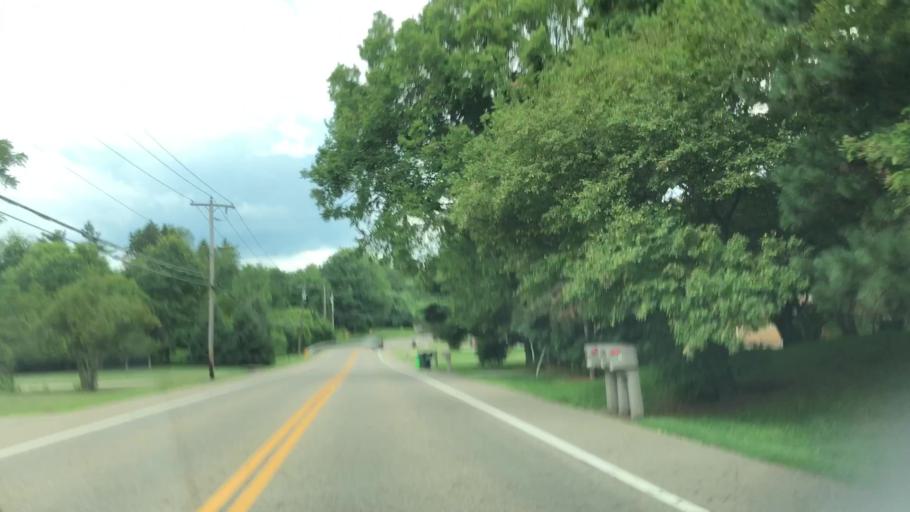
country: US
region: Ohio
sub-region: Summit County
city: New Franklin
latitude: 40.9537
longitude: -81.5209
